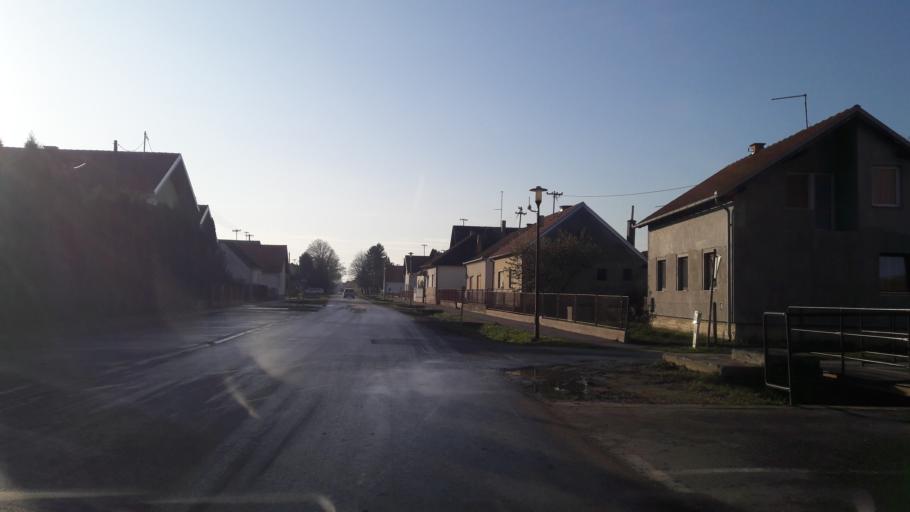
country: HR
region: Osjecko-Baranjska
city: Darda
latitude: 45.6275
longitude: 18.6976
